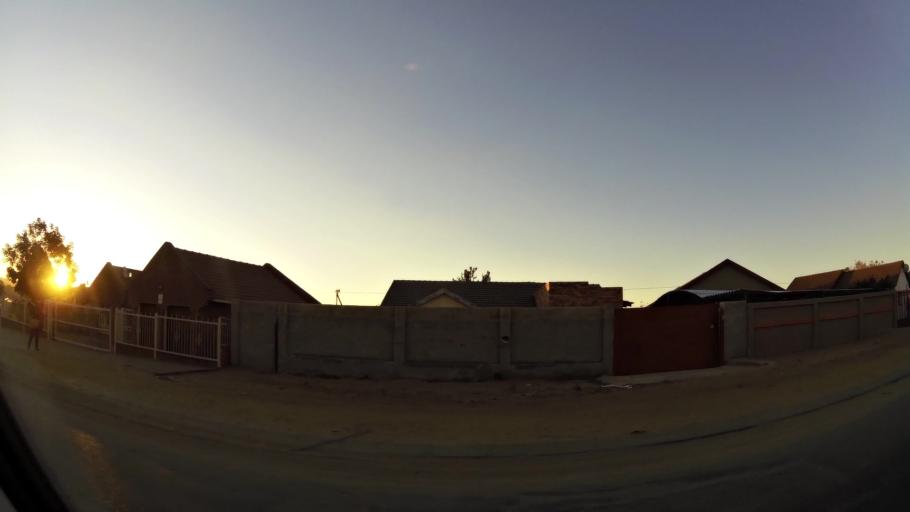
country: ZA
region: Limpopo
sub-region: Capricorn District Municipality
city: Polokwane
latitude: -23.8575
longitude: 29.3729
